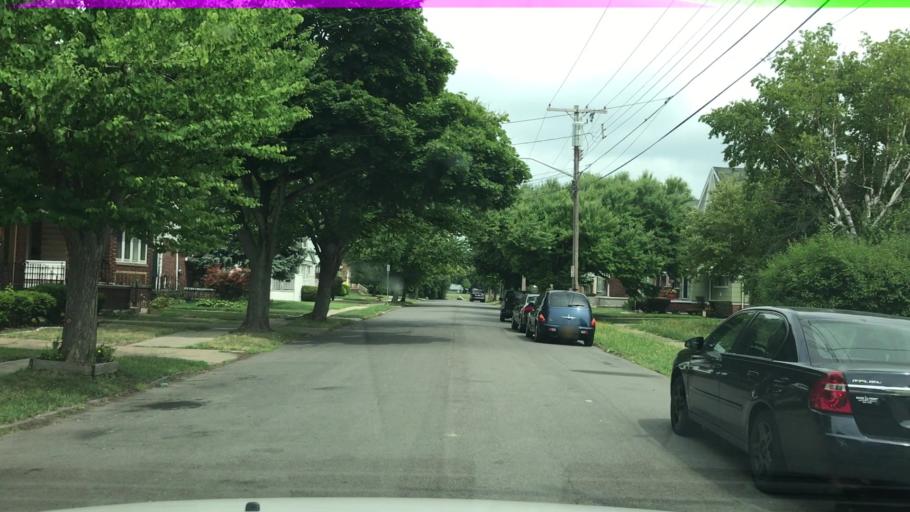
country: US
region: New York
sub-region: Erie County
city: Sloan
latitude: 42.9103
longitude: -78.8016
